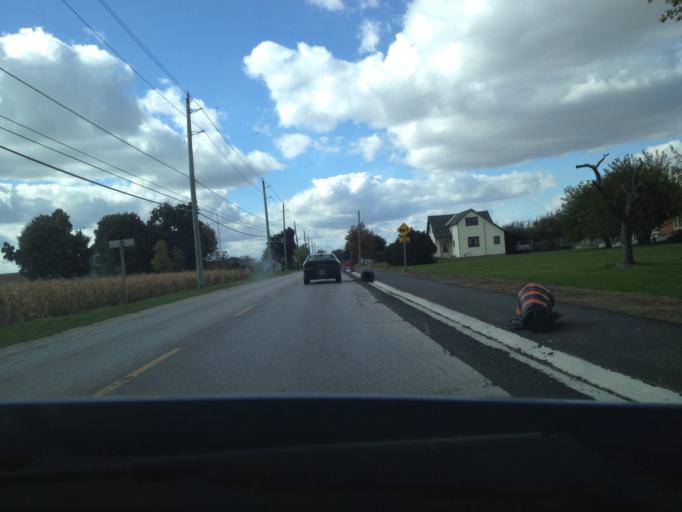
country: CA
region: Ontario
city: Amherstburg
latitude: 42.0348
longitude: -82.6233
